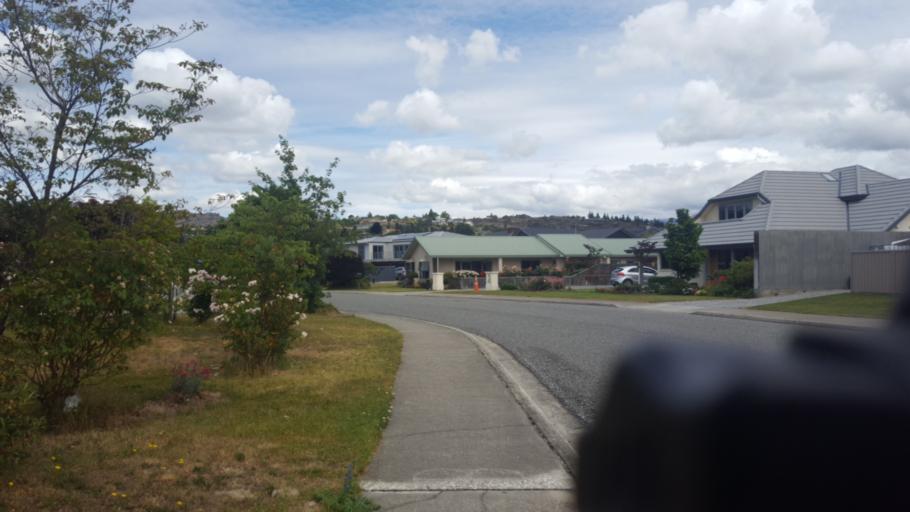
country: NZ
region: Otago
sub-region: Queenstown-Lakes District
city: Wanaka
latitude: -45.2517
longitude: 169.3832
